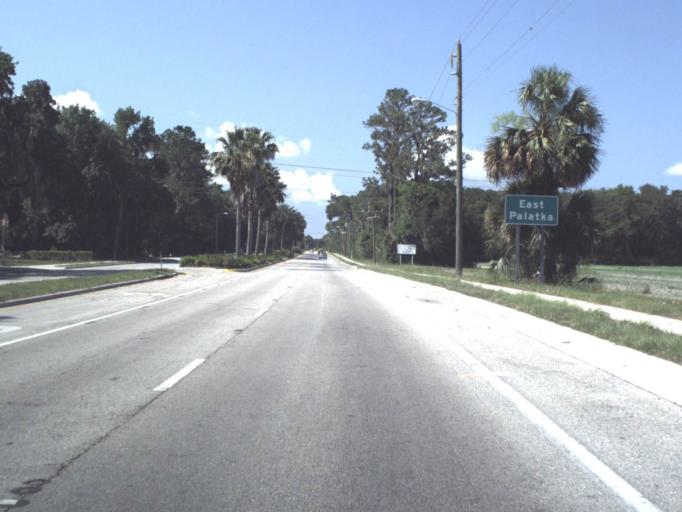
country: US
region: Florida
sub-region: Putnam County
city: East Palatka
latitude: 29.6634
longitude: -81.5938
